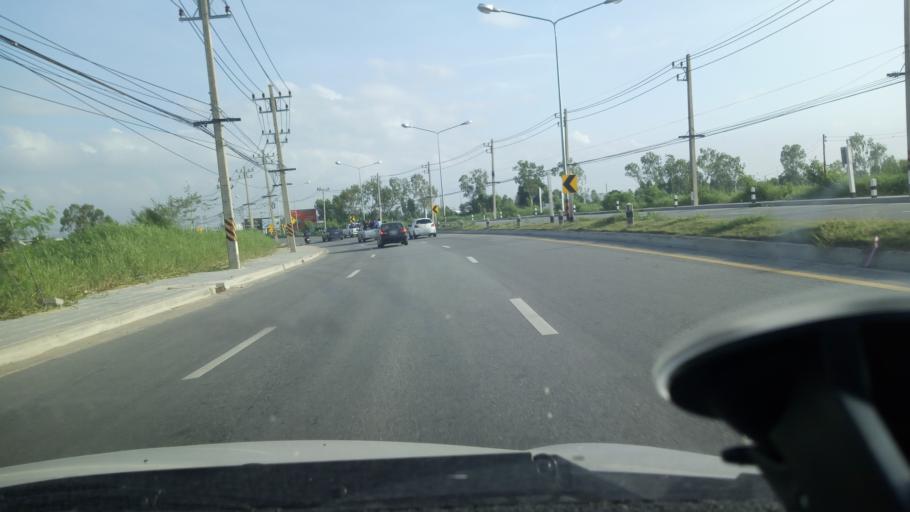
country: TH
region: Chon Buri
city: Phan Thong
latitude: 13.4404
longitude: 101.1056
